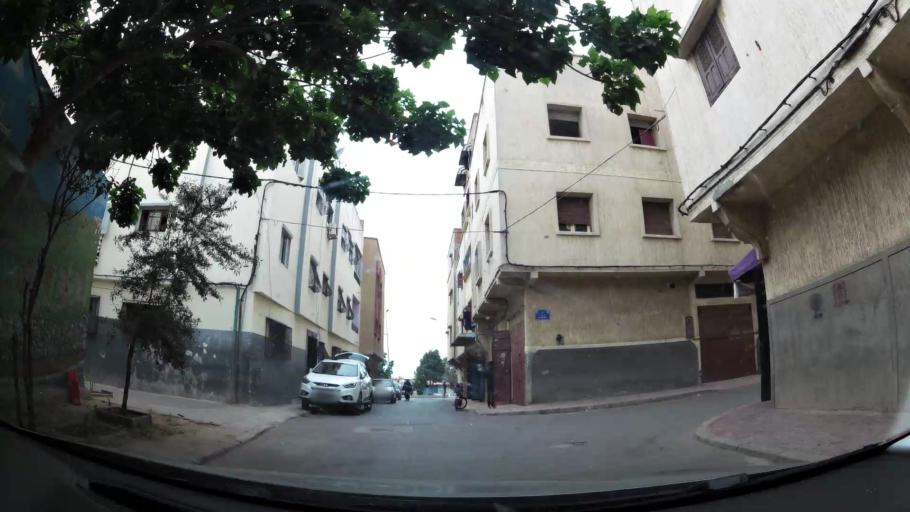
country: MA
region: Rabat-Sale-Zemmour-Zaer
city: Sale
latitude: 34.0291
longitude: -6.8054
